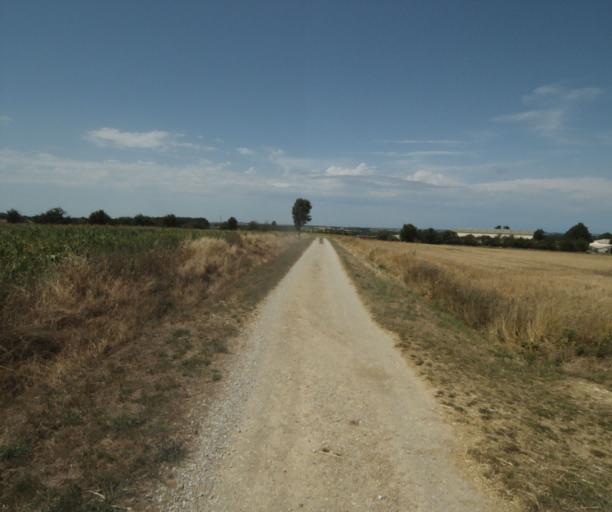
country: FR
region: Midi-Pyrenees
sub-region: Departement de la Haute-Garonne
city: Saint-Felix-Lauragais
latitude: 43.4523
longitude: 1.8560
